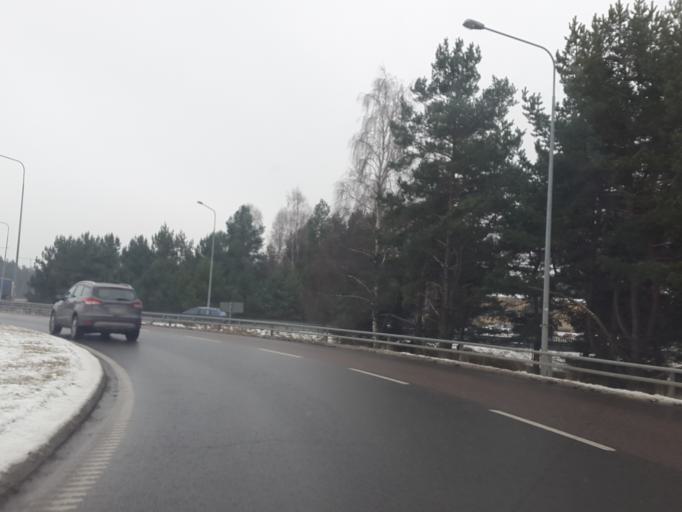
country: SE
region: Joenkoeping
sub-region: Jonkopings Kommun
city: Jonkoping
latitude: 57.7600
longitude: 14.1563
